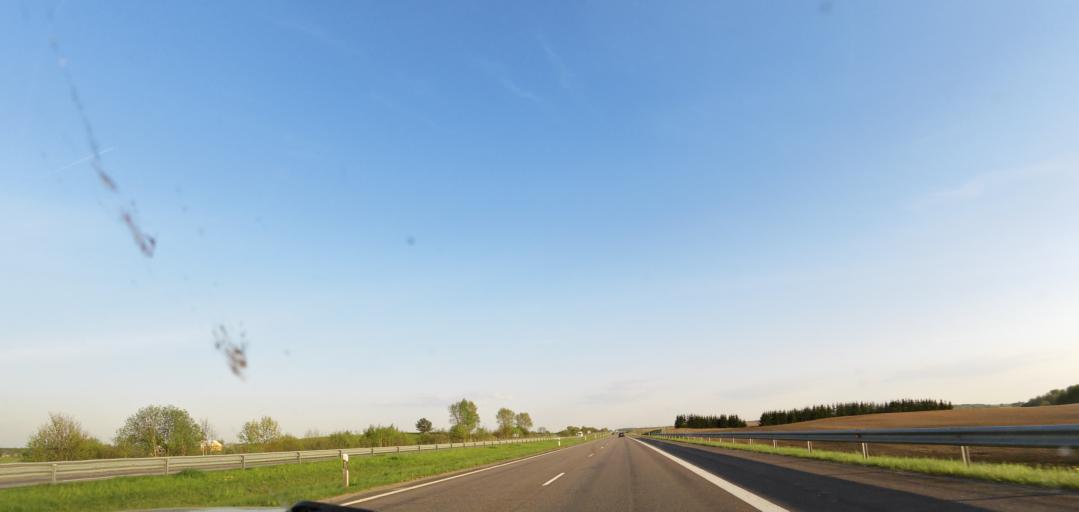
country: LT
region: Vilnius County
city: Ukmerge
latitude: 55.1752
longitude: 24.8124
